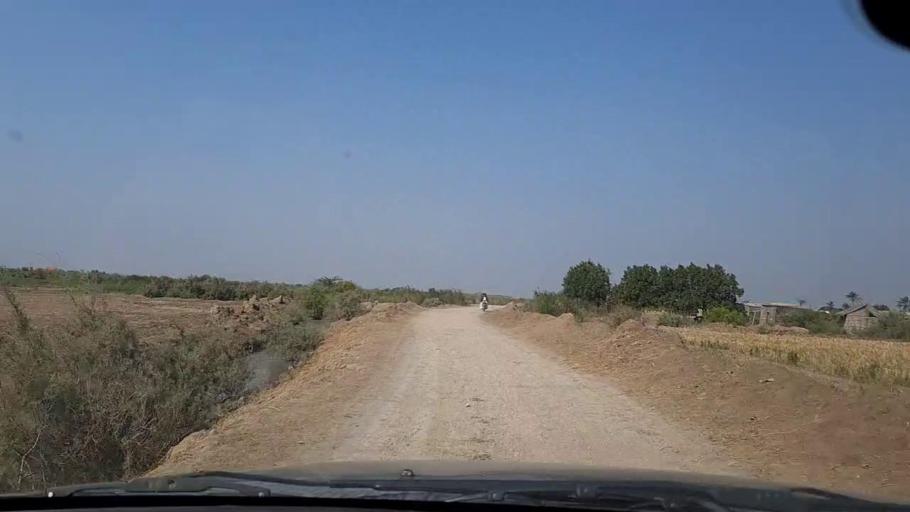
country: PK
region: Sindh
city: Mirpur Sakro
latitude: 24.3588
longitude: 67.6831
